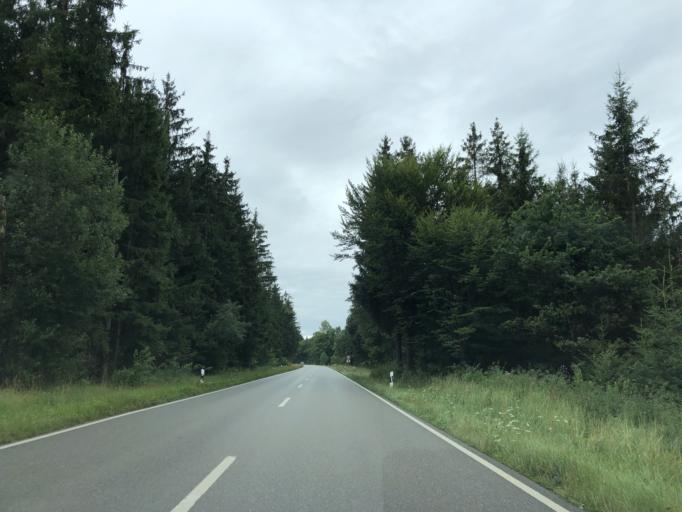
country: DE
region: Bavaria
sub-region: Upper Bavaria
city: Taufkirchen
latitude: 48.0124
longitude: 11.6373
